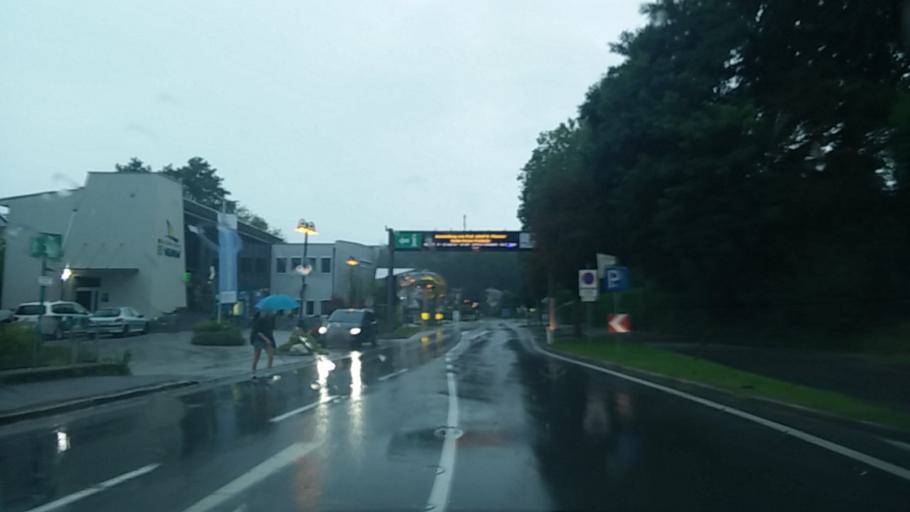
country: AT
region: Carinthia
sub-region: Politischer Bezirk Villach Land
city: Velden am Woerthersee
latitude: 46.6138
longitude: 14.0369
